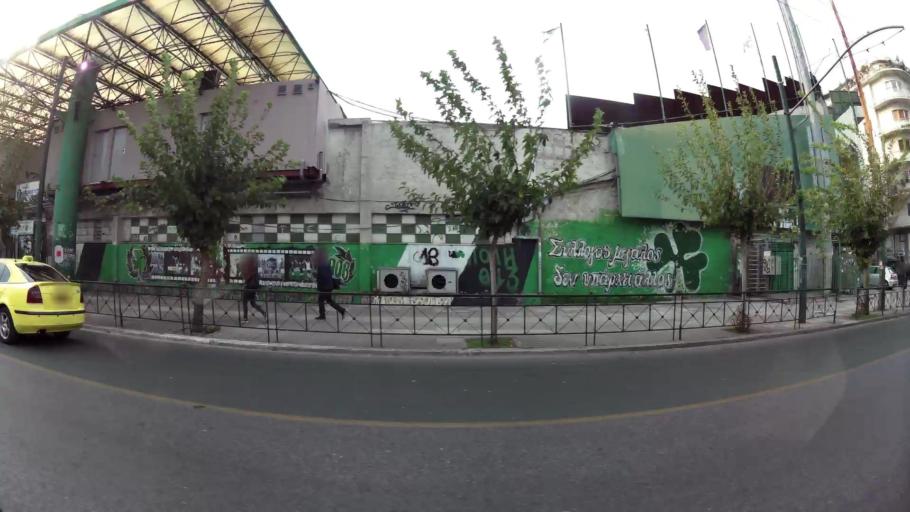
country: GR
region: Attica
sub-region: Nomarchia Athinas
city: Kipseli
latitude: 37.9878
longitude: 23.7540
